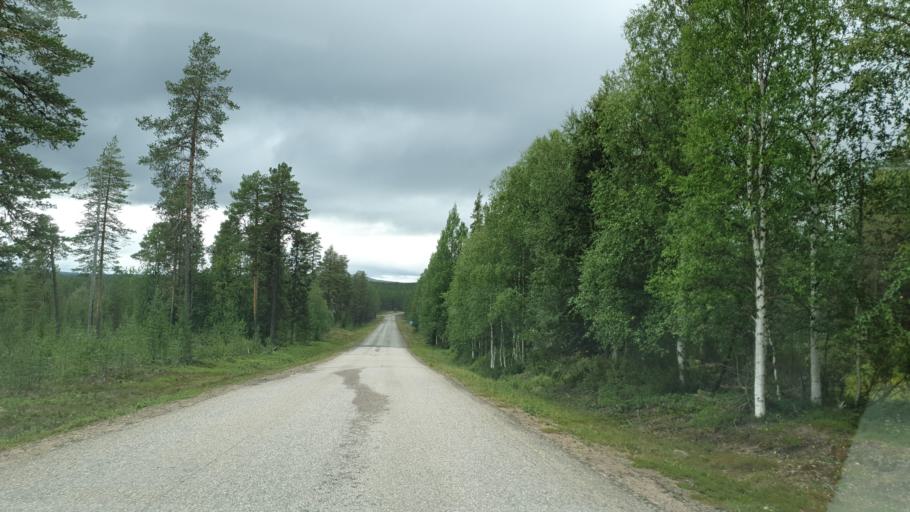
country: FI
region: Lapland
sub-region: Tunturi-Lappi
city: Kolari
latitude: 67.5327
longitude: 23.9932
